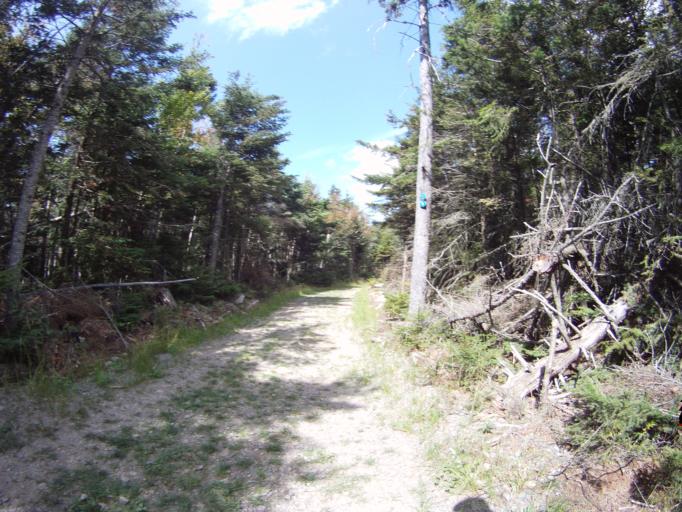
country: US
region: New York
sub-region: Ulster County
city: Woodstock
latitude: 42.1856
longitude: -74.2321
